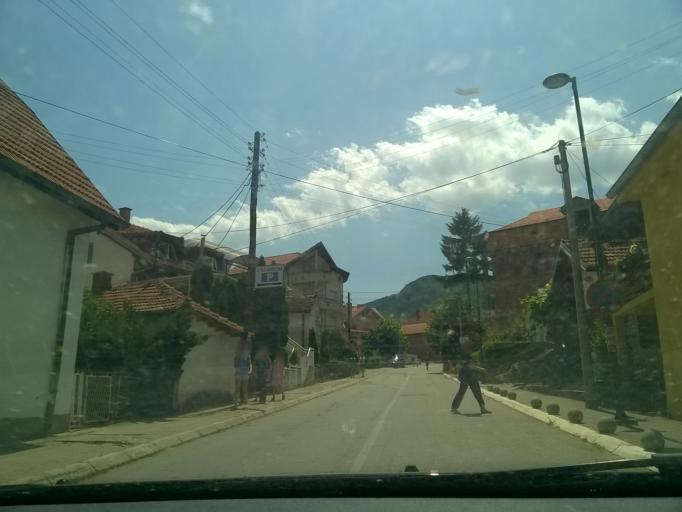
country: RS
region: Central Serbia
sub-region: Zajecarski Okrug
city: Soko Banja
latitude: 43.6444
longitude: 21.8774
